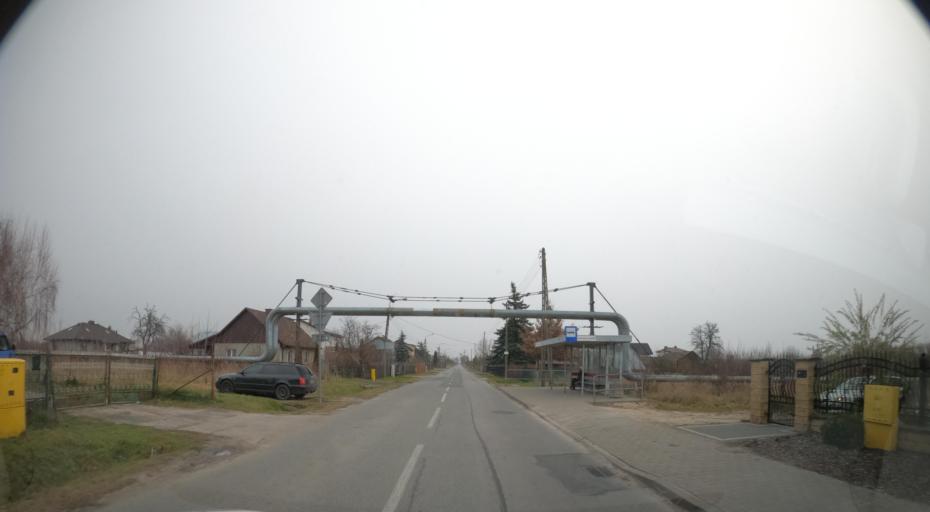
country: PL
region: Masovian Voivodeship
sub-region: Radom
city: Radom
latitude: 51.4376
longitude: 21.1884
